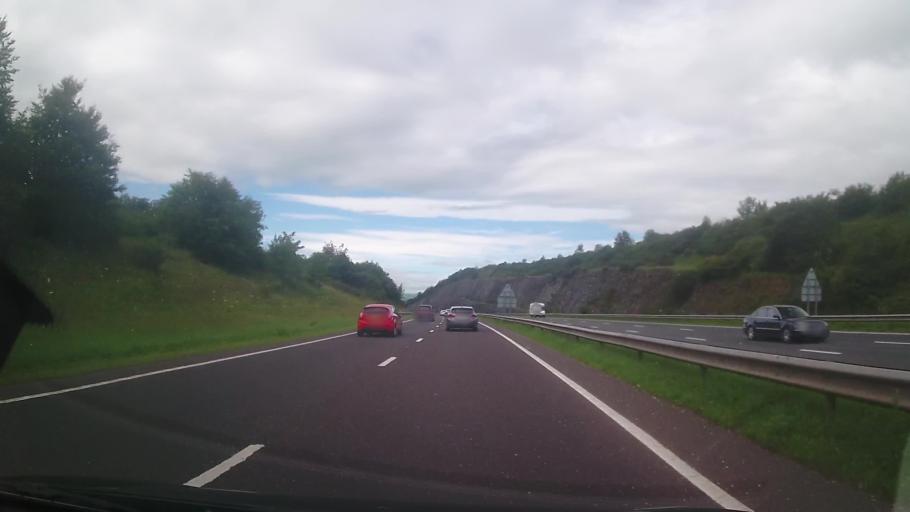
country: GB
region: Wales
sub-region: Denbighshire
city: Cwm
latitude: 53.2728
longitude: -3.3689
